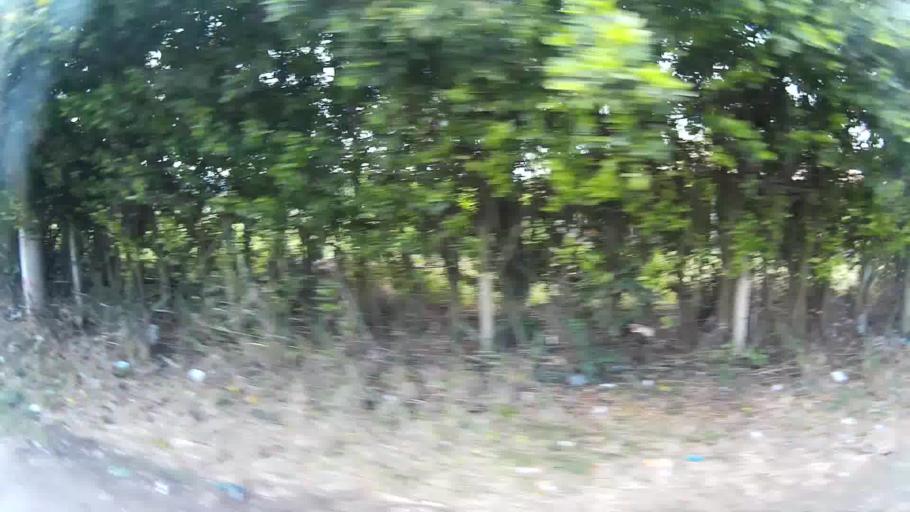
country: CO
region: Risaralda
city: La Virginia
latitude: 4.8290
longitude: -75.8455
